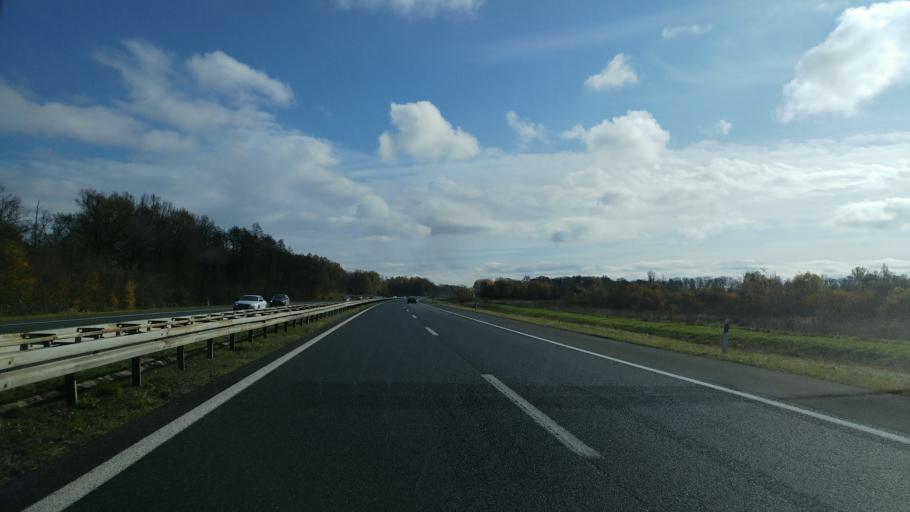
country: HR
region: Zagrebacka
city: Lupoglav
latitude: 45.7446
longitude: 16.3205
